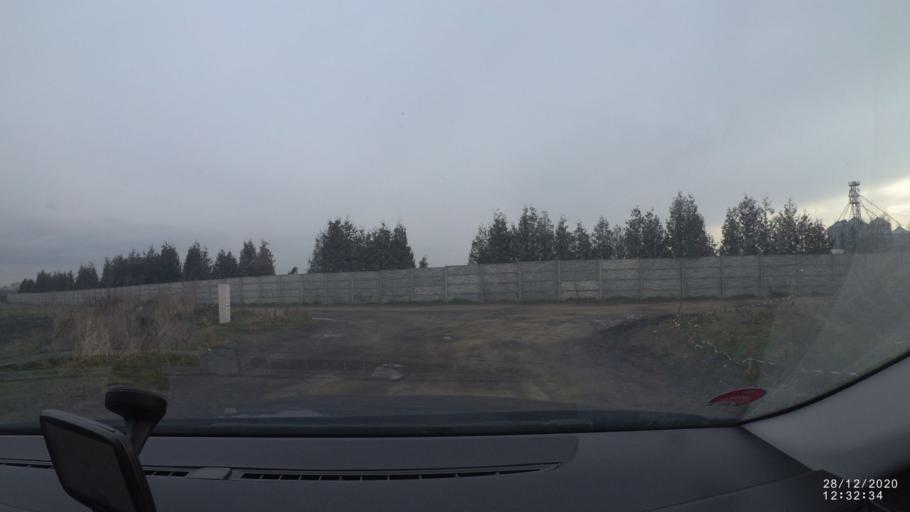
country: CZ
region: Central Bohemia
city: Kostelec nad Labem
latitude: 50.2029
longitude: 14.5940
